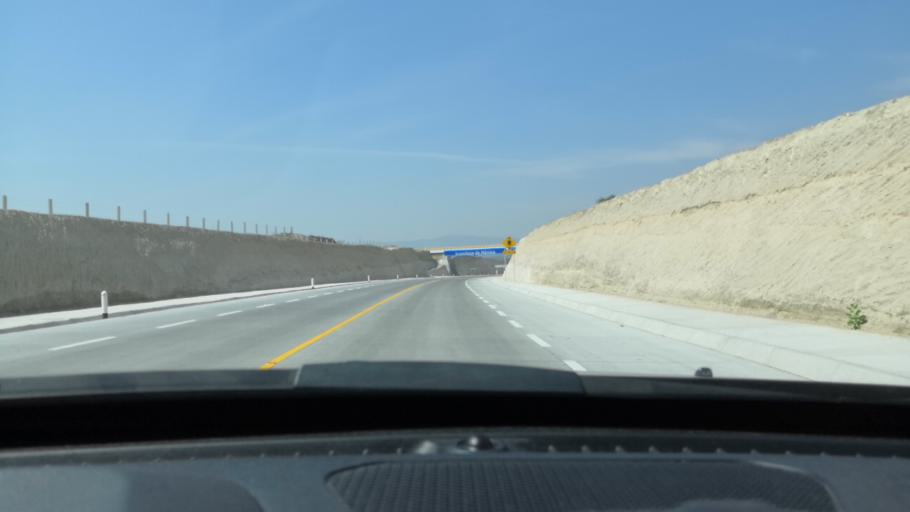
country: MX
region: Guanajuato
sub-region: Leon
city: Malagana (San Antonio del Monte)
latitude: 21.0899
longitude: -101.7938
